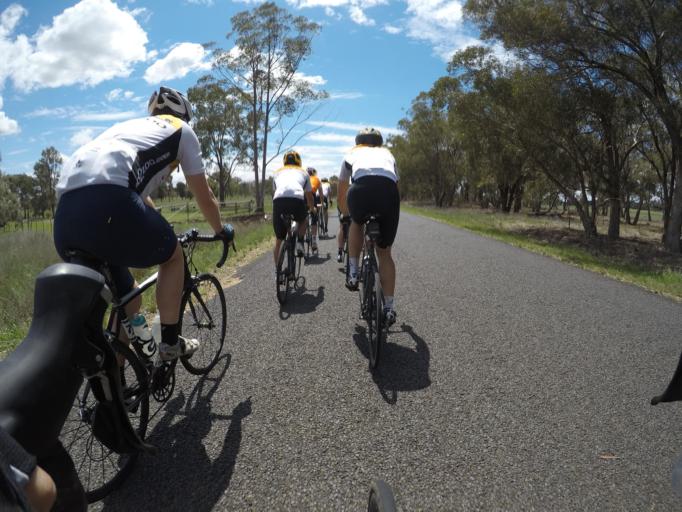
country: AU
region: New South Wales
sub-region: Dubbo Municipality
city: Dubbo
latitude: -32.3483
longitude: 148.5963
